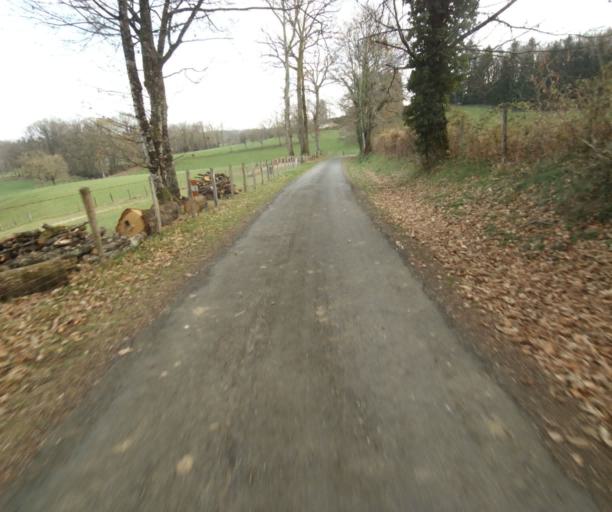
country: FR
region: Limousin
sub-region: Departement de la Correze
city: Saint-Clement
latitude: 45.3594
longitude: 1.6444
